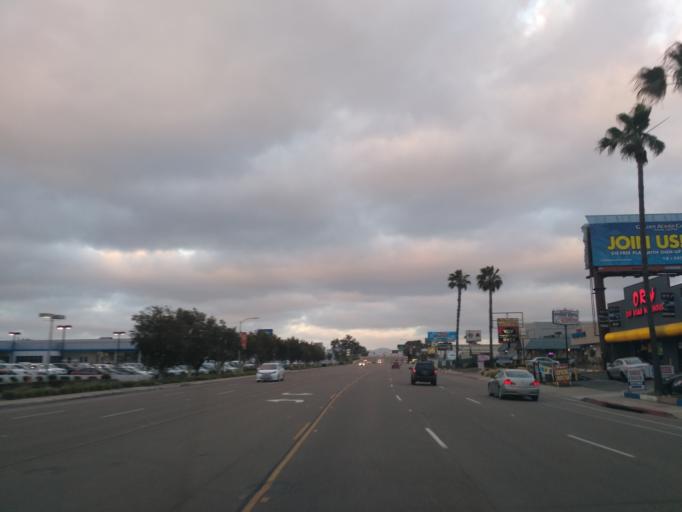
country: US
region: California
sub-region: San Diego County
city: San Diego
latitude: 32.8217
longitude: -117.1534
